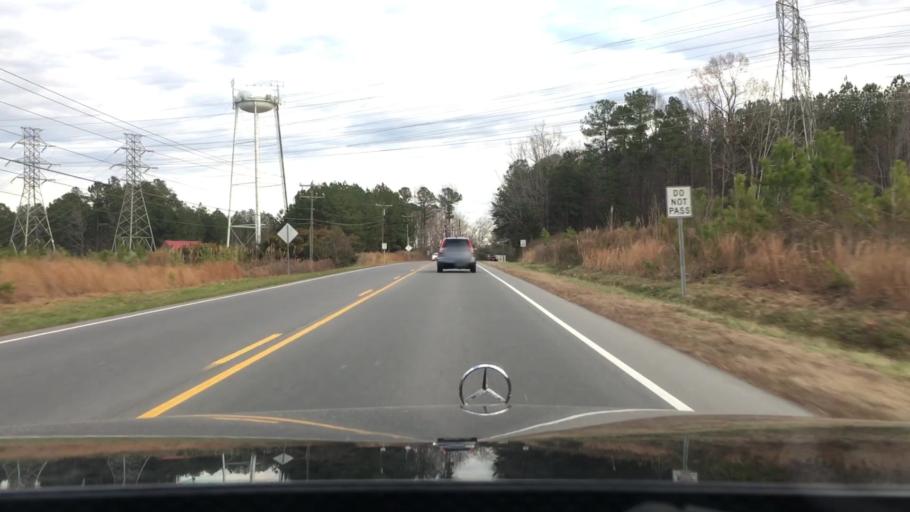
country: US
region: North Carolina
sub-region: Orange County
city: Hillsborough
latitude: 36.0440
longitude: -79.0188
